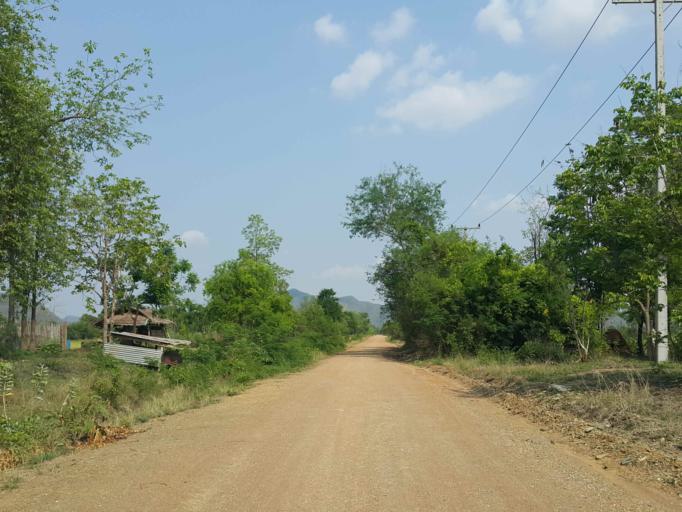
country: TH
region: Sukhothai
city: Thung Saliam
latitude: 17.3353
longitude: 99.4282
